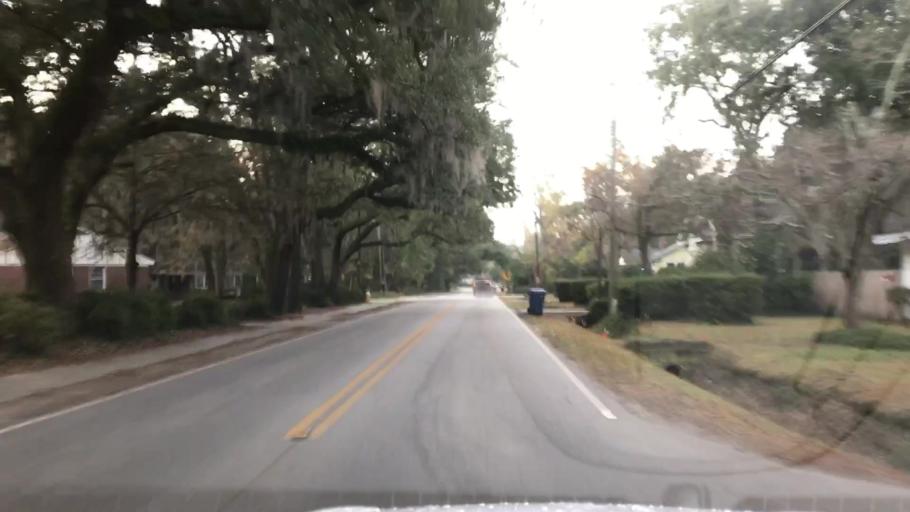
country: US
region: South Carolina
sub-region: Charleston County
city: North Charleston
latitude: 32.8015
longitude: -80.0071
